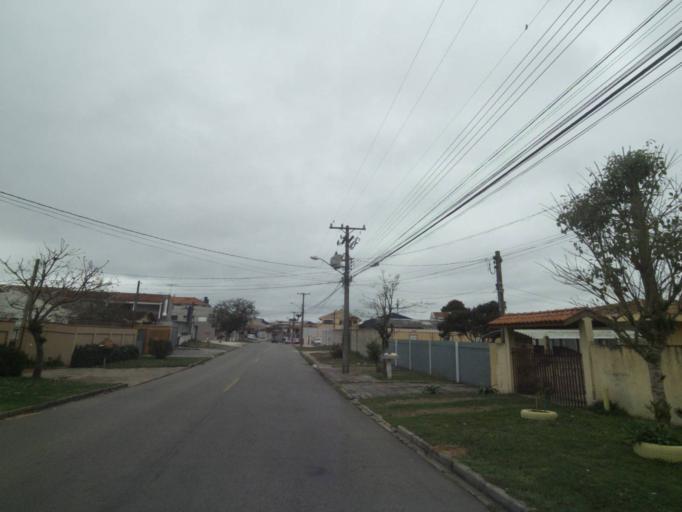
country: BR
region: Parana
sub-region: Curitiba
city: Curitiba
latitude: -25.4988
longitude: -49.2903
